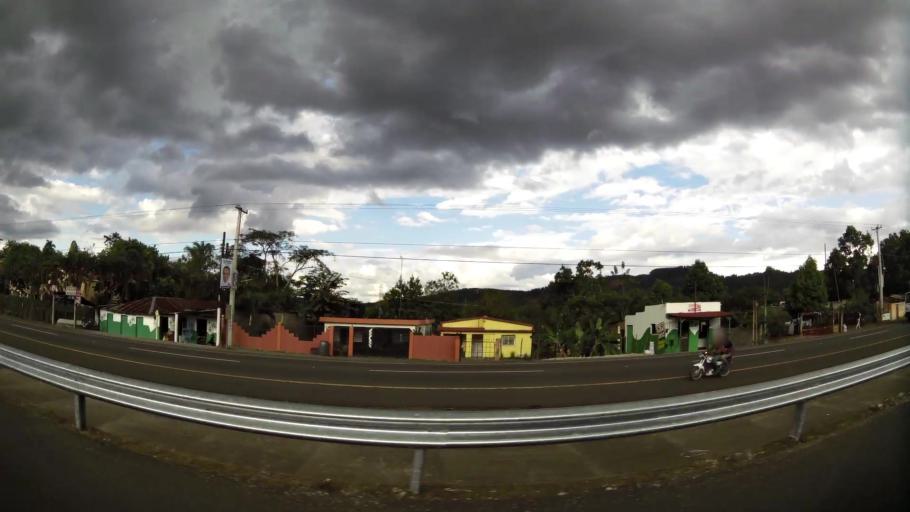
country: DO
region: Monsenor Nouel
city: Bonao
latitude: 18.9893
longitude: -70.4308
